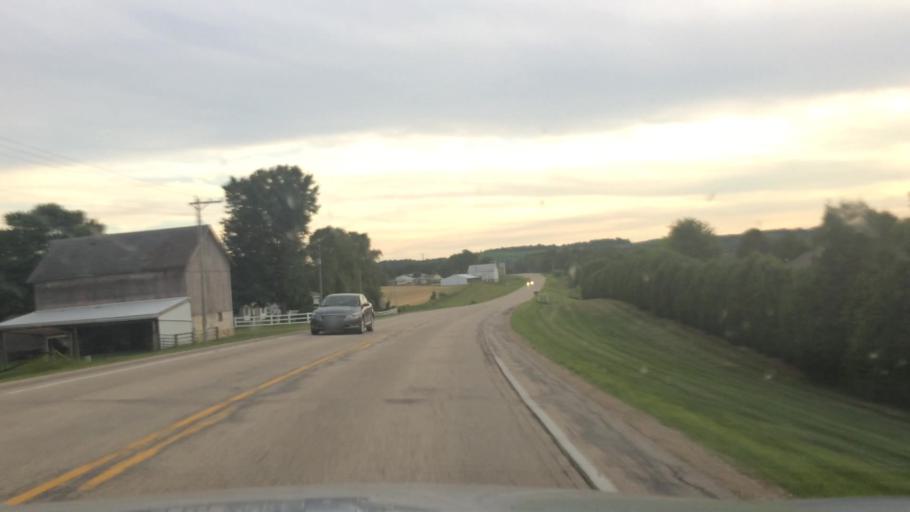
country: US
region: Wisconsin
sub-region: Dane County
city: Waunakee
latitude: 43.1981
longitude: -89.5541
